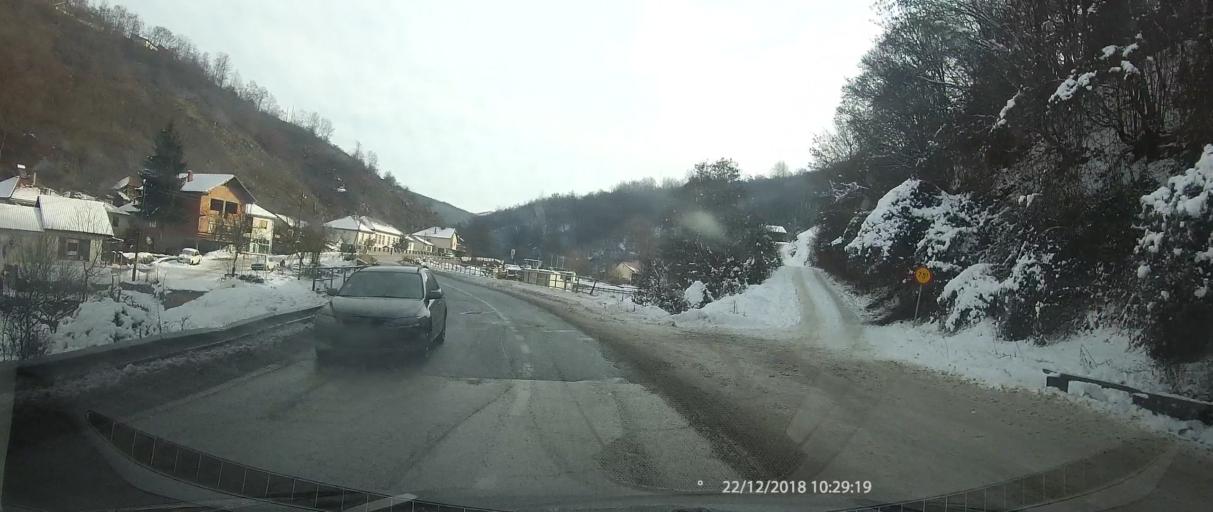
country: MK
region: Kriva Palanka
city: Kriva Palanka
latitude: 42.2235
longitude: 22.3949
